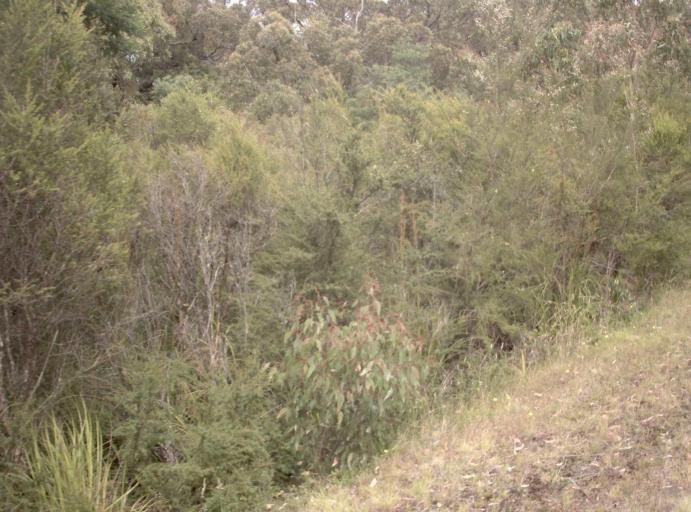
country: AU
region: Victoria
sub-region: Latrobe
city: Traralgon
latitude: -38.0714
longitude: 146.4299
